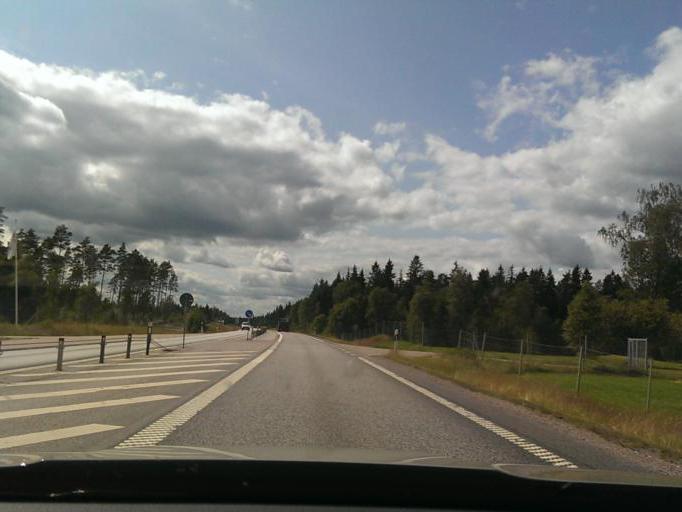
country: SE
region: Joenkoeping
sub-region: Varnamo Kommun
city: Varnamo
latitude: 57.1841
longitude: 13.9807
